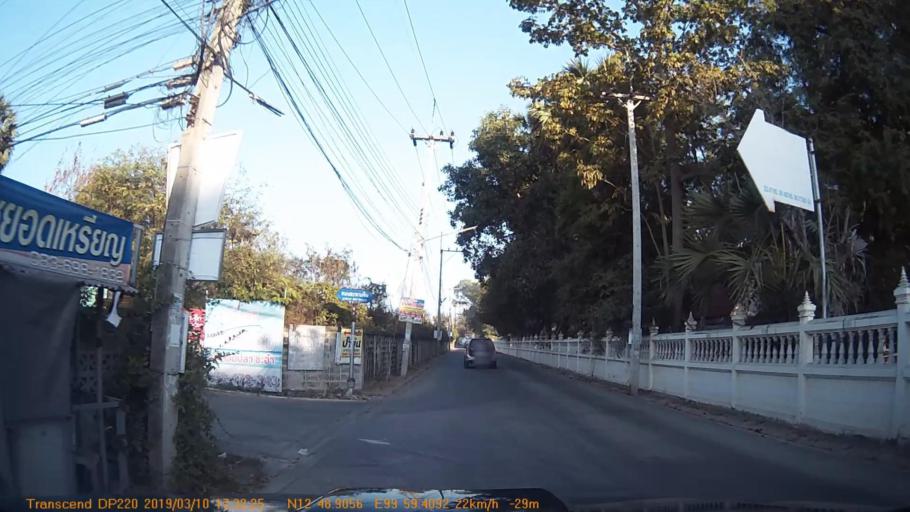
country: TH
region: Phetchaburi
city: Cha-am
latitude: 12.8151
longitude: 99.9902
